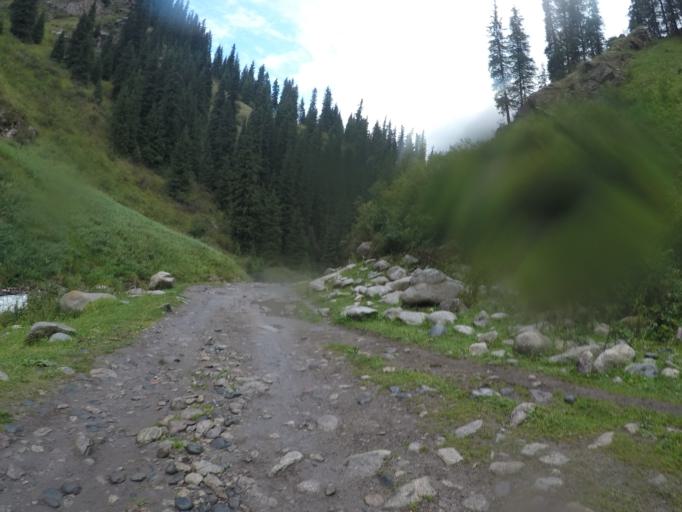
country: KG
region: Ysyk-Koel
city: Teploklyuchenka
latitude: 42.4151
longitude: 78.5713
